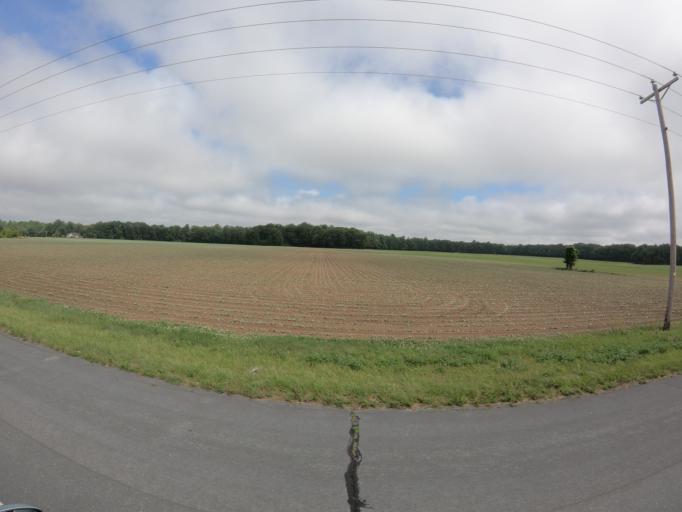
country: US
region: Delaware
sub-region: Kent County
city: Riverview
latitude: 39.0081
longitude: -75.5217
